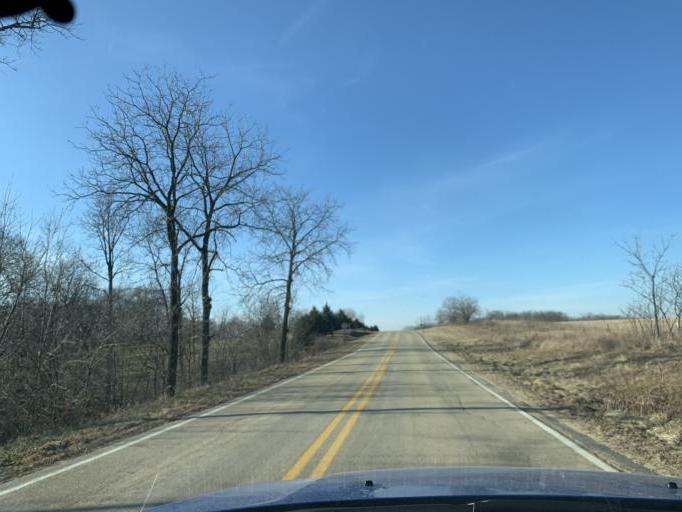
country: US
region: Wisconsin
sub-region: Iowa County
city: Barneveld
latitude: 42.8136
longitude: -89.9035
